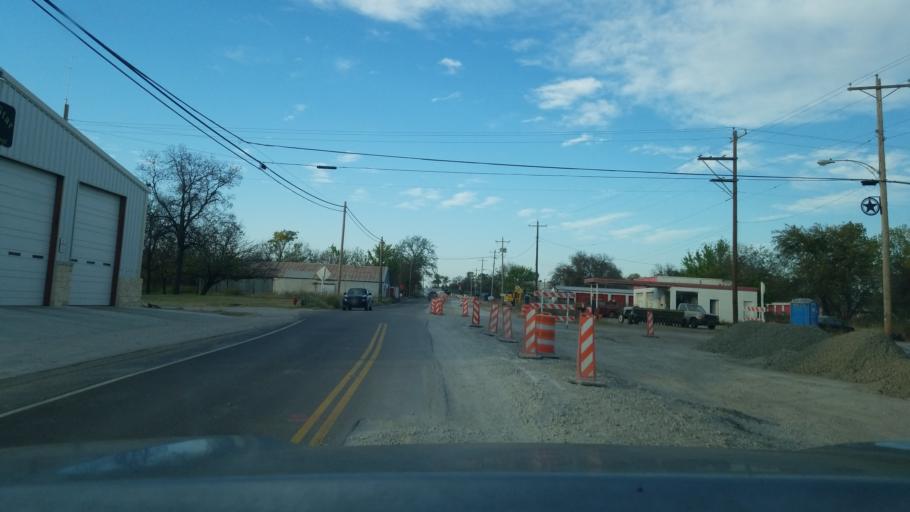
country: US
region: Texas
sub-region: Brown County
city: Lake Brownwood
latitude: 32.0966
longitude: -98.9640
